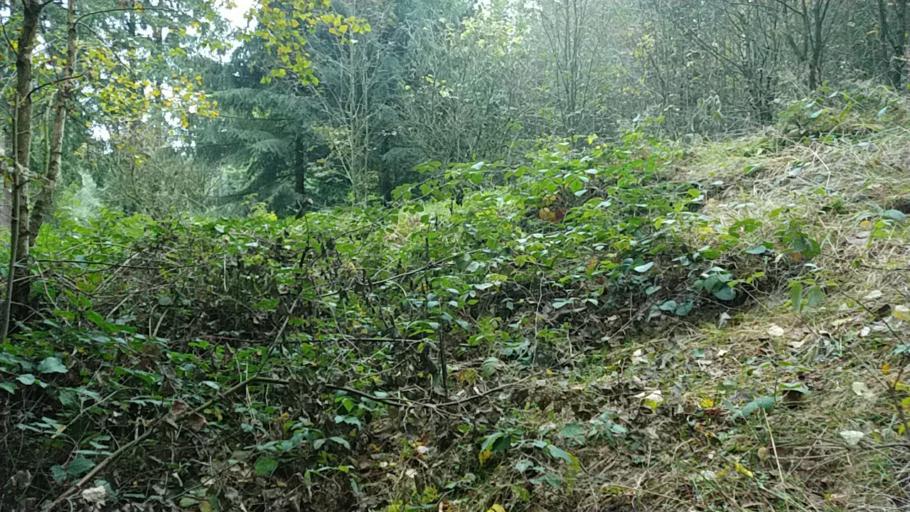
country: DE
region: Lower Saxony
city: Nienstadt
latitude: 52.2676
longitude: 9.1938
